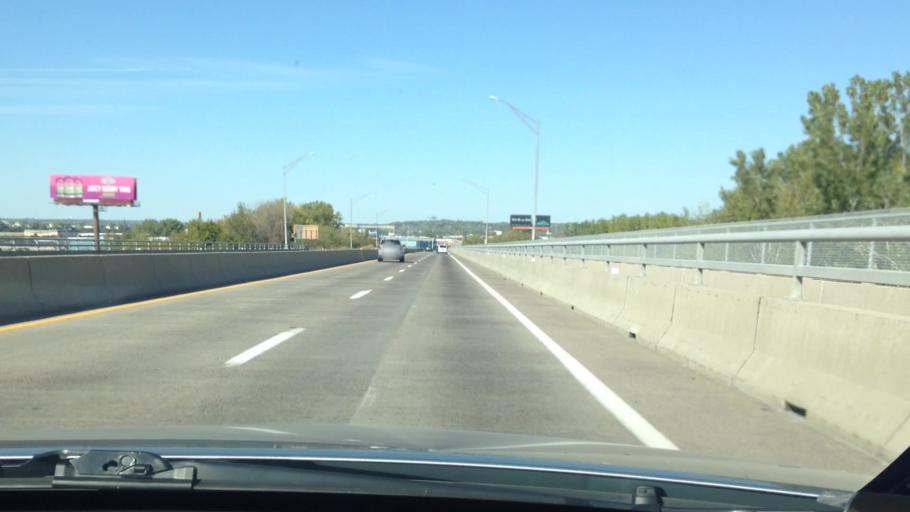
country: US
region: Missouri
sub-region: Jackson County
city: Kansas City
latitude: 39.1187
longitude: -94.5792
